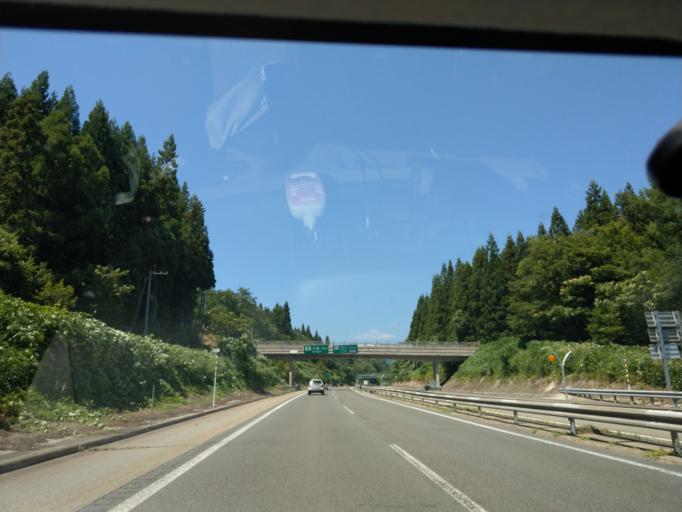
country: JP
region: Akita
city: Omagari
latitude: 39.4105
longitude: 140.4417
